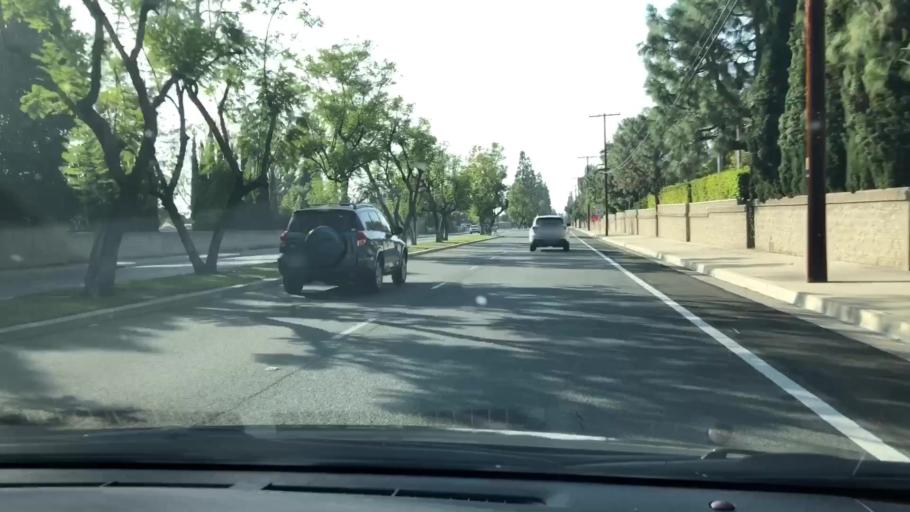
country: US
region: California
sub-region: Orange County
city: Villa Park
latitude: 33.8107
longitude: -117.8140
